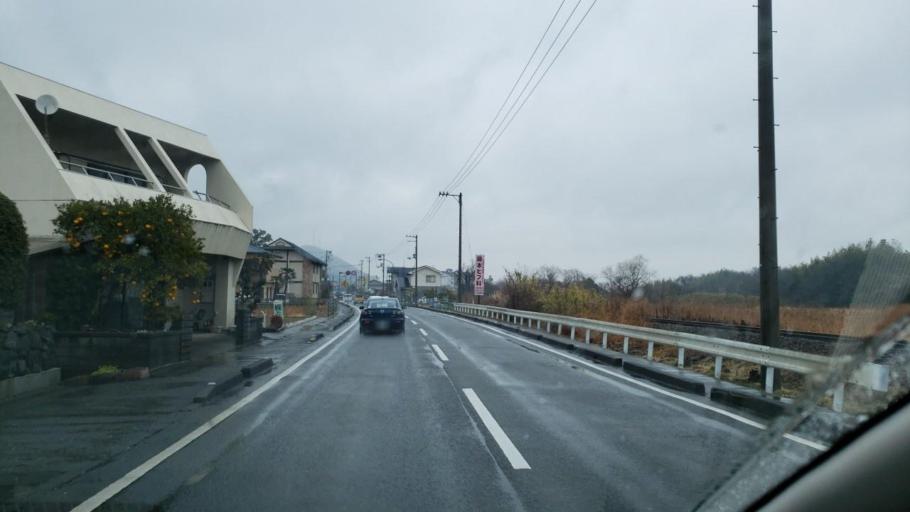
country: JP
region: Tokushima
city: Narutocho-mitsuishi
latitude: 34.1566
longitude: 134.5333
